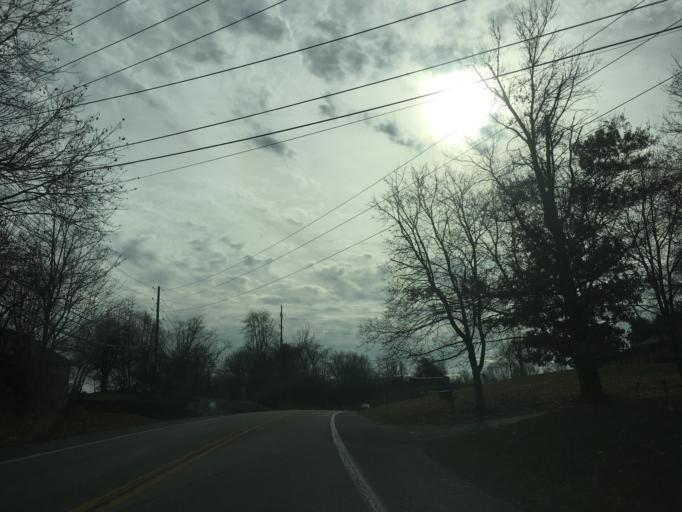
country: US
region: Pennsylvania
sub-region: Dauphin County
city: Colonial Park
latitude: 40.3150
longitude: -76.8220
